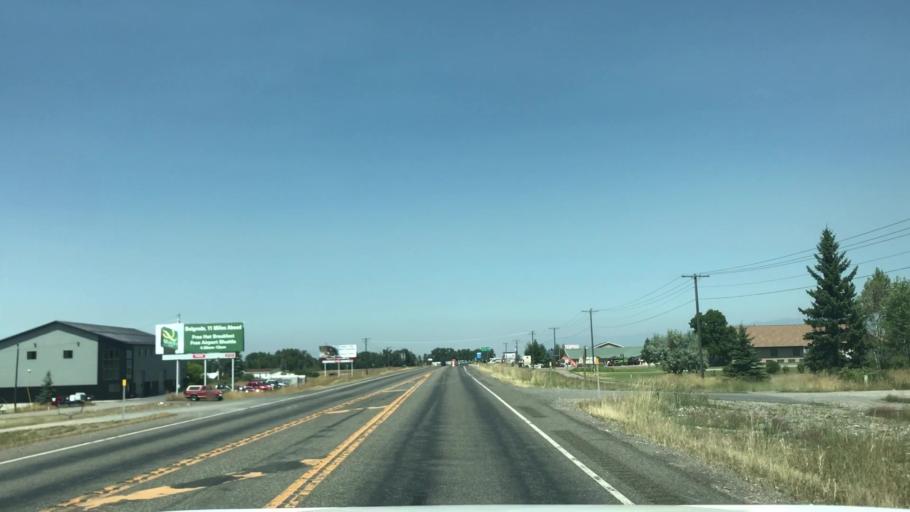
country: US
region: Montana
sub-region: Gallatin County
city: Four Corners
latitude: 45.6003
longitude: -111.1963
